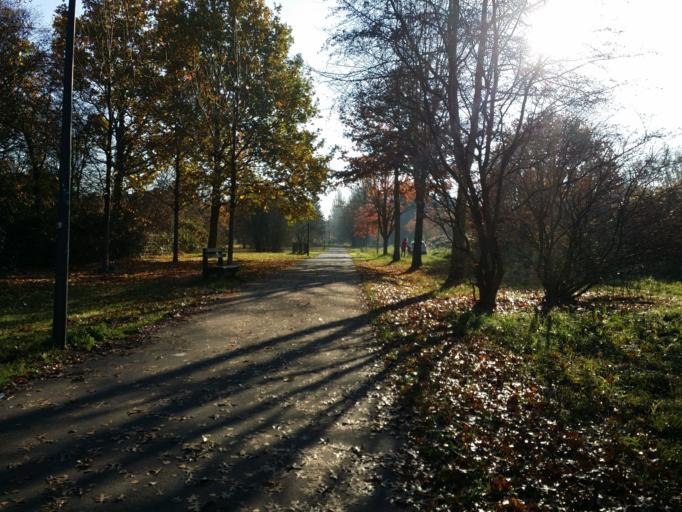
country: DE
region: Bremen
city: Bremen
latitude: 53.0688
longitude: 8.8779
